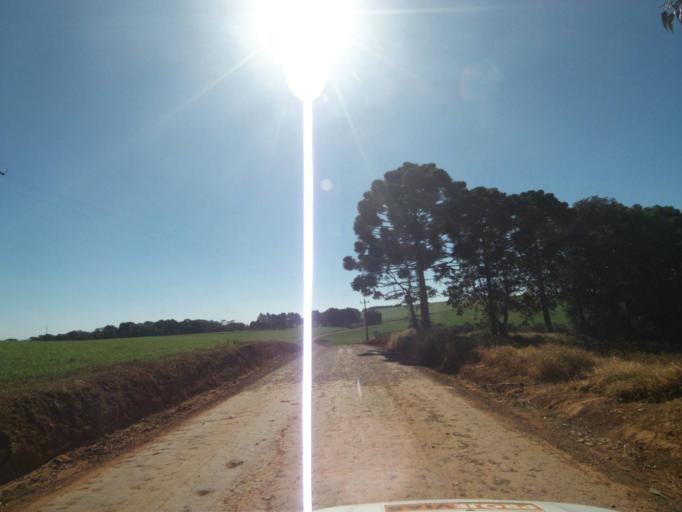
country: BR
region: Parana
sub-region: Tibagi
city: Tibagi
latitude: -24.6119
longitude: -50.6056
